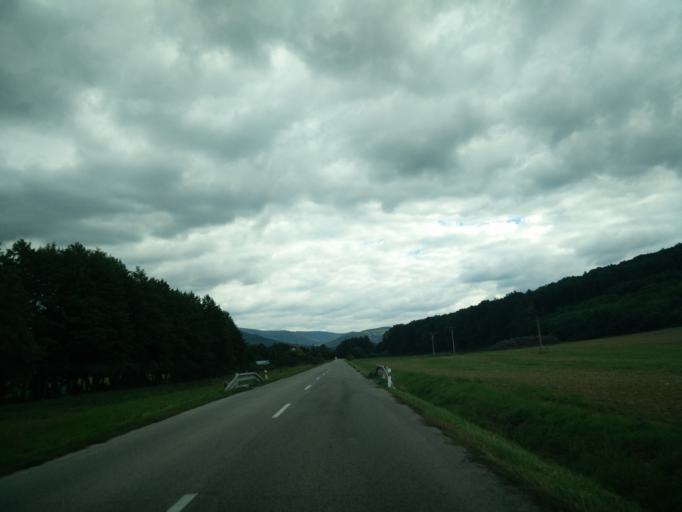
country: SK
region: Nitriansky
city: Partizanske
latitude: 48.6226
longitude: 18.4601
